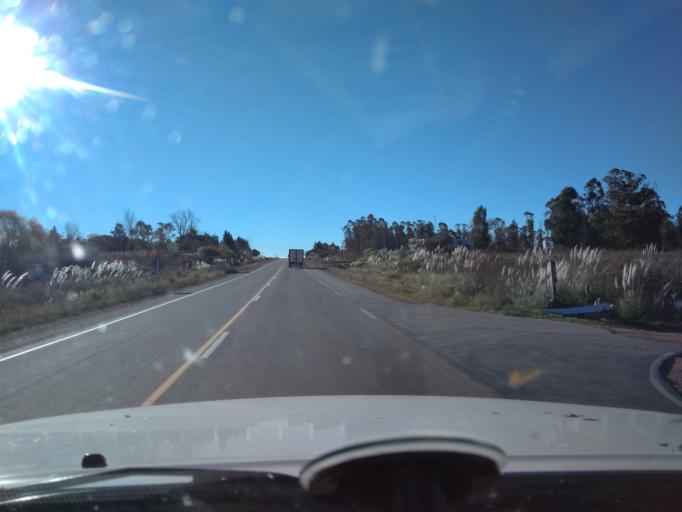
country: UY
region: Canelones
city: Sauce
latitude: -34.5936
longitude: -56.0520
